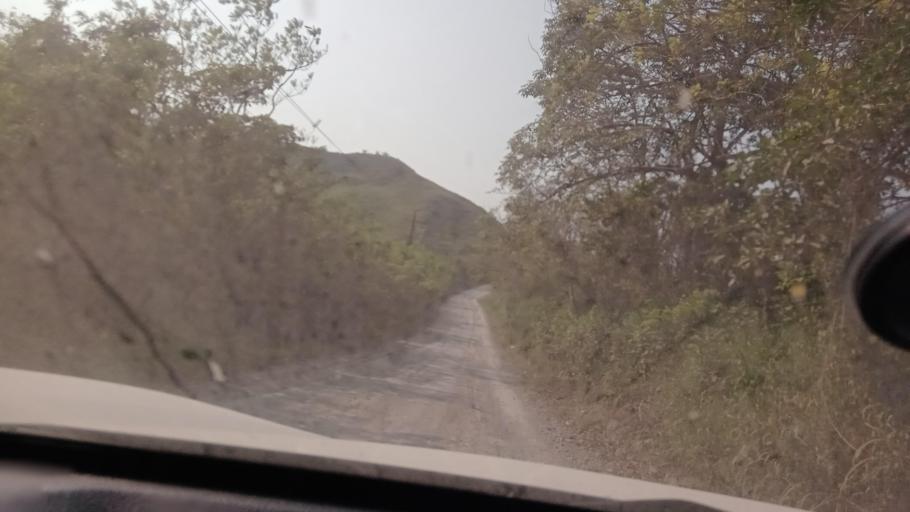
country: MX
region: Tabasco
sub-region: Huimanguillo
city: Francisco Rueda
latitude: 17.6132
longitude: -93.9378
